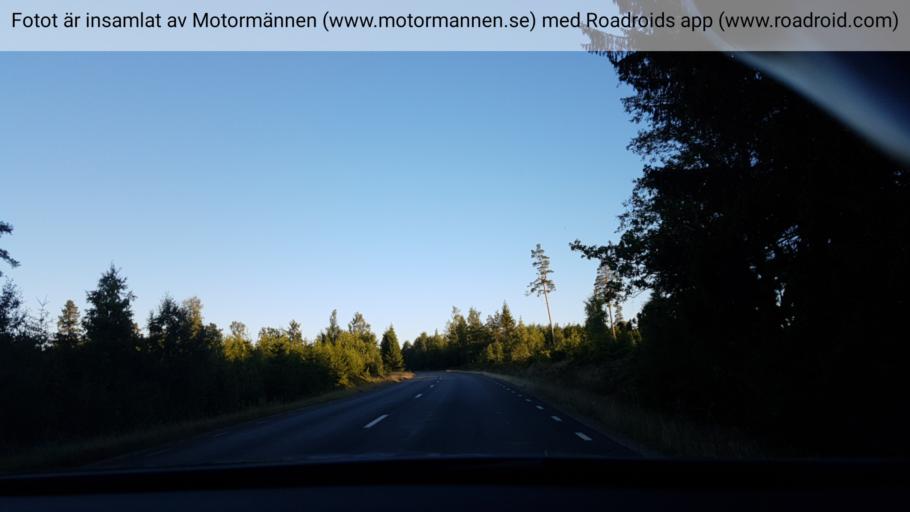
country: SE
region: Vaestra Goetaland
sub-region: Hjo Kommun
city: Hjo
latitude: 58.3895
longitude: 14.3522
